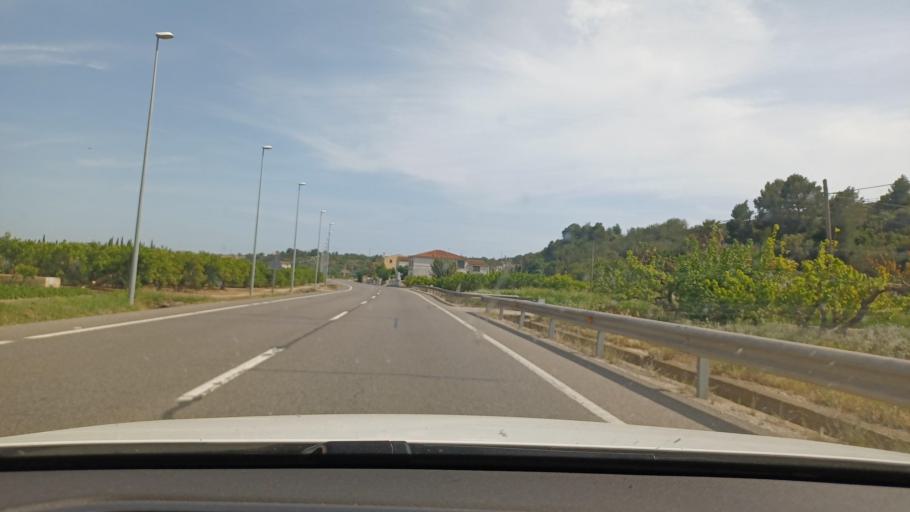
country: ES
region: Catalonia
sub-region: Provincia de Tarragona
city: Tortosa
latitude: 40.7818
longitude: 0.5038
